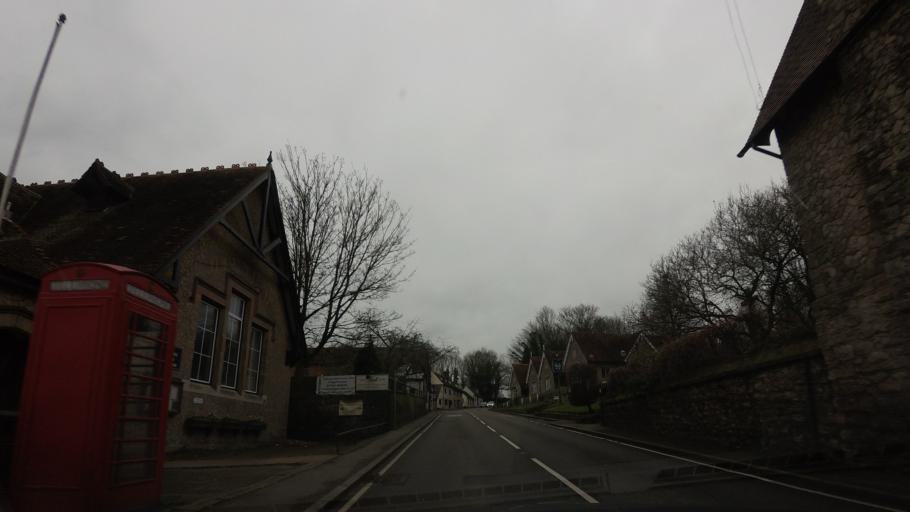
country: GB
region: England
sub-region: Kent
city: Maidstone
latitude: 51.2234
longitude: 0.5107
